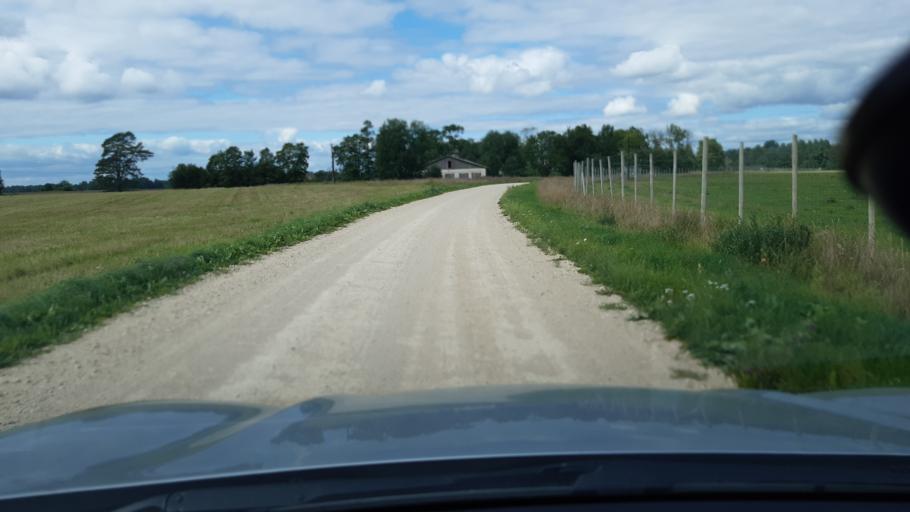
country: EE
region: Paernumaa
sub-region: Vaendra vald (alev)
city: Vandra
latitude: 58.7777
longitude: 25.0548
